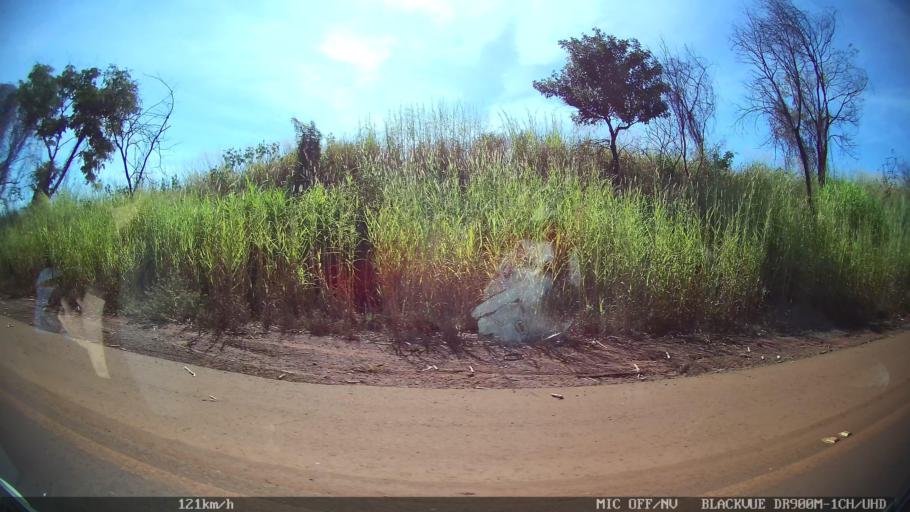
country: BR
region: Sao Paulo
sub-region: Sao Joaquim Da Barra
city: Sao Joaquim da Barra
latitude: -20.5480
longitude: -47.7611
